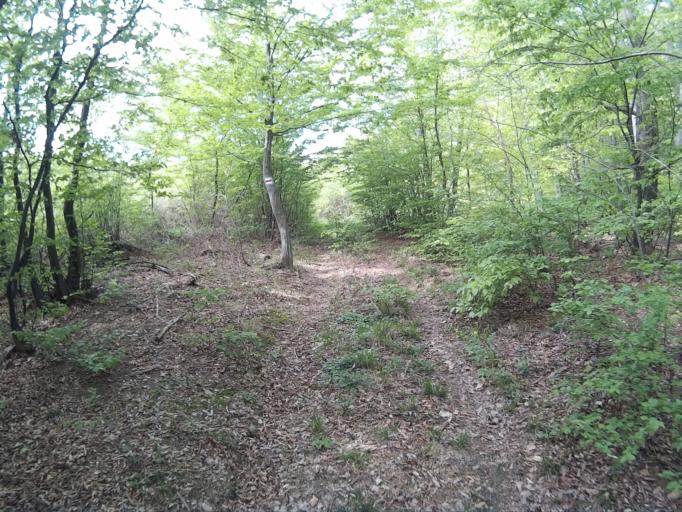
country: HU
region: Vas
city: Koszeg
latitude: 47.3649
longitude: 16.5037
